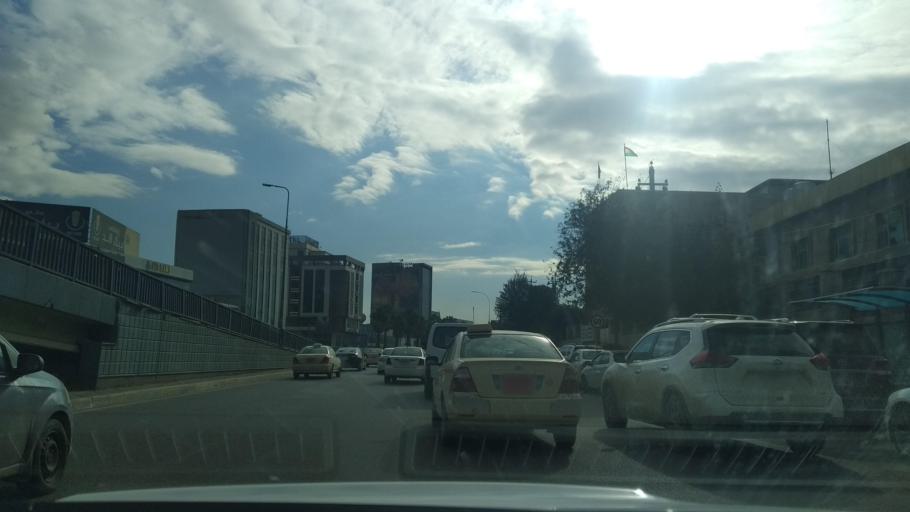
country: IQ
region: Arbil
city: Erbil
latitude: 36.2005
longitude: 44.0210
